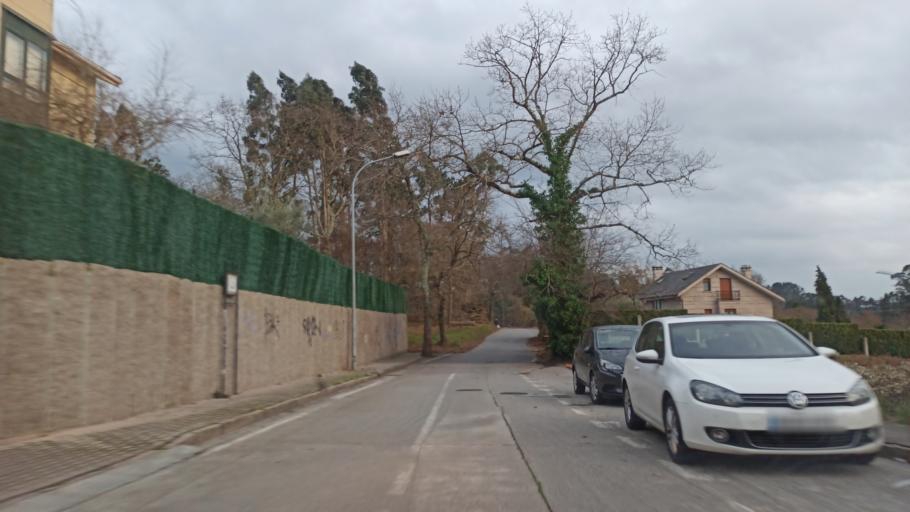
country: ES
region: Galicia
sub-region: Provincia da Coruna
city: Cambre
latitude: 43.3270
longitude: -8.3489
